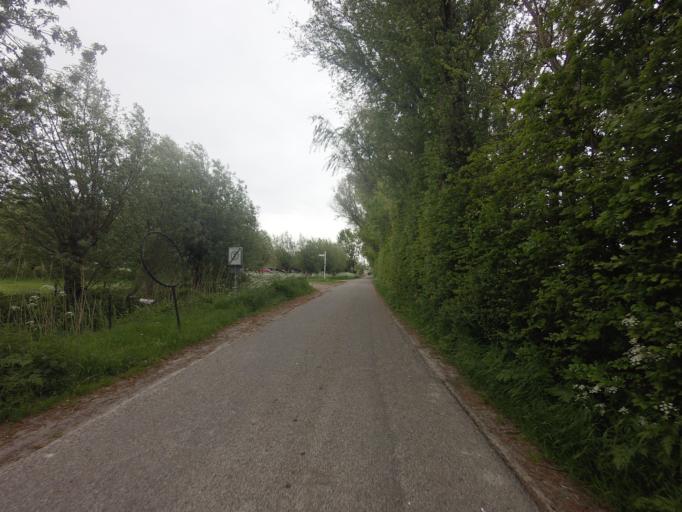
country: NL
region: Zeeland
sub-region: Gemeente Middelburg
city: Middelburg
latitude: 51.5227
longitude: 3.5727
